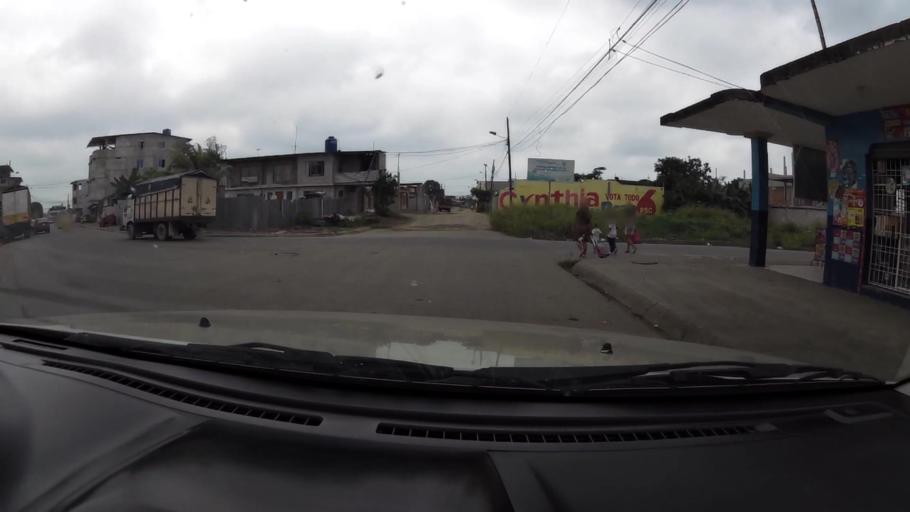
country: EC
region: El Oro
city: Pasaje
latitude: -3.2434
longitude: -79.8349
